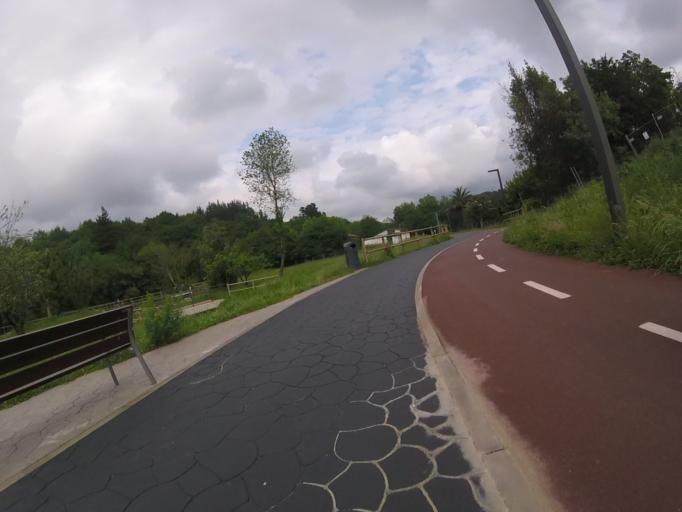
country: ES
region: Basque Country
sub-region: Provincia de Guipuzcoa
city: San Sebastian
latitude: 43.3047
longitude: -1.9574
